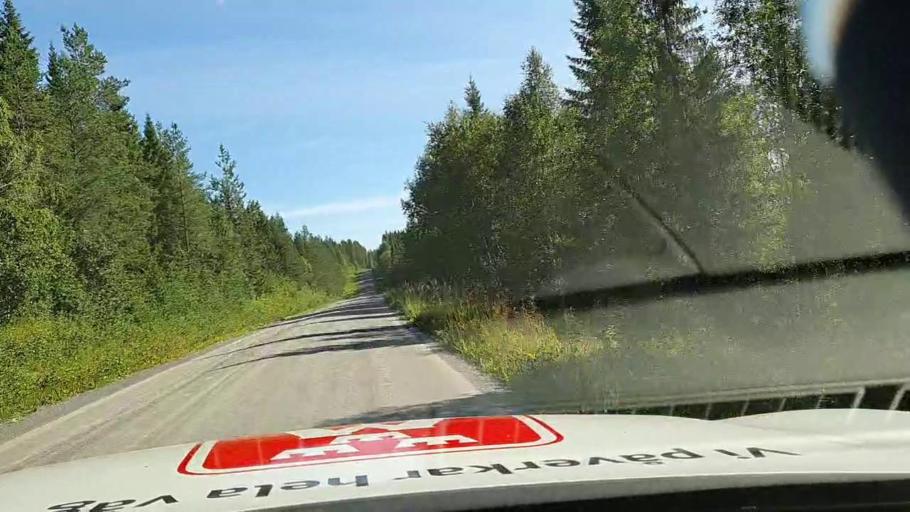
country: SE
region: Jaemtland
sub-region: Krokoms Kommun
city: Krokom
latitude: 63.6878
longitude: 14.5715
